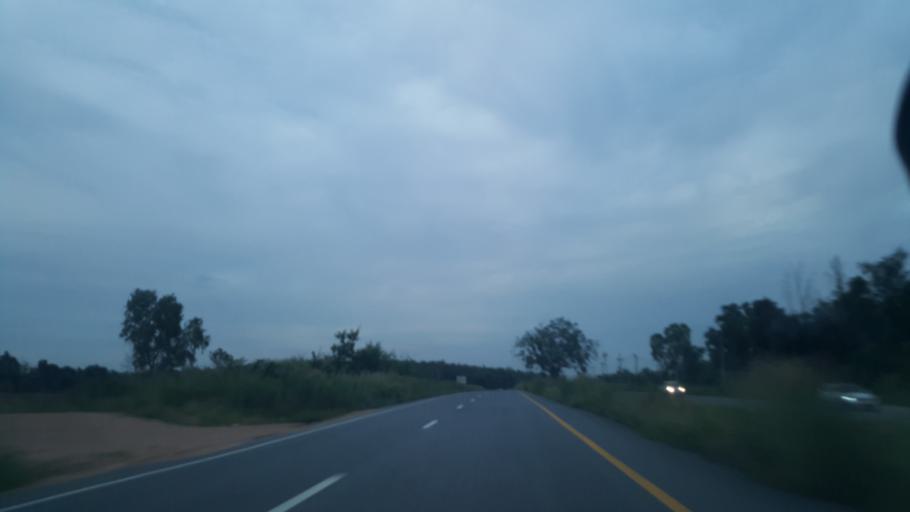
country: TH
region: Rayong
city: Ban Chang
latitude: 12.8662
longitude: 101.0241
